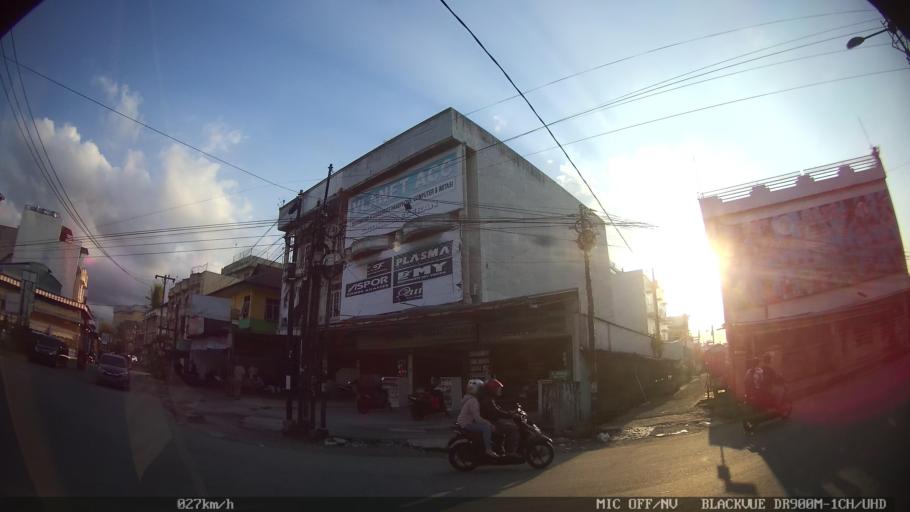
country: ID
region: North Sumatra
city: Medan
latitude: 3.5966
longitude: 98.6639
